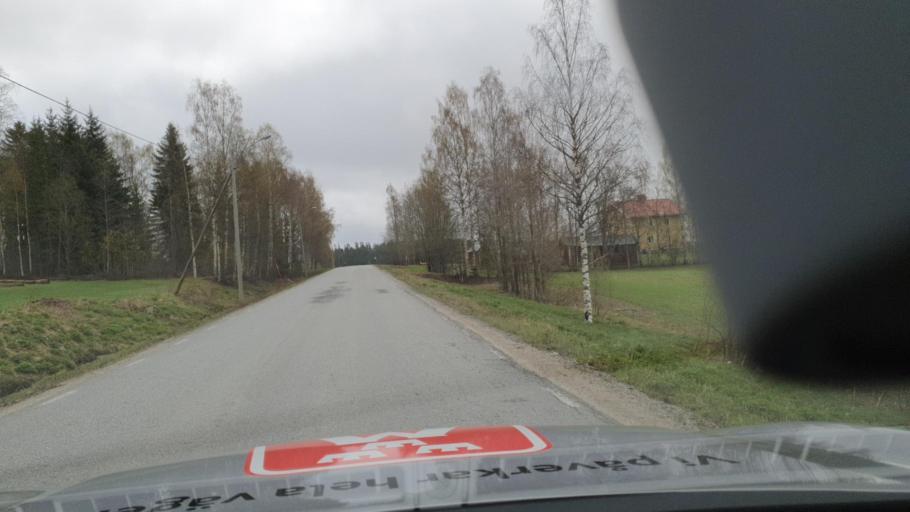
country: SE
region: Vaesternorrland
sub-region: OErnskoeldsviks Kommun
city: Husum
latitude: 63.5740
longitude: 19.0326
